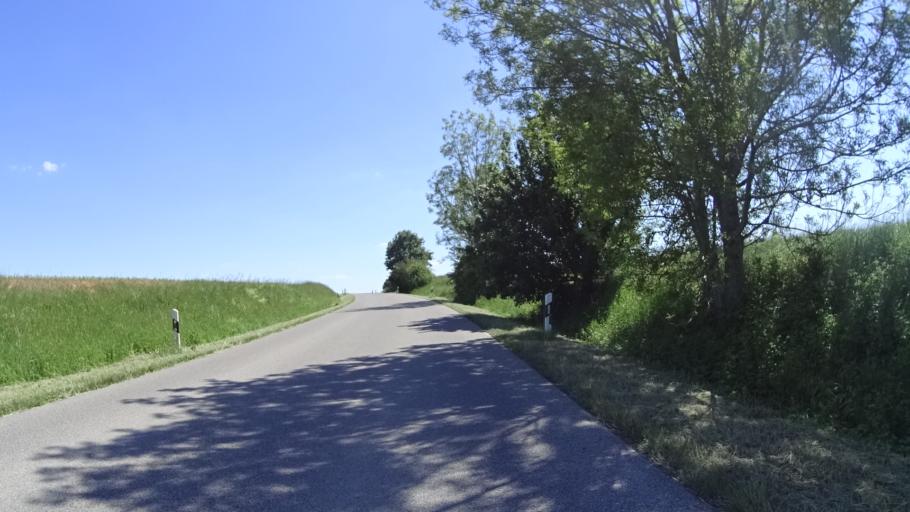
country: DE
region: Bavaria
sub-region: Regierungsbezirk Mittelfranken
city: Gebsattel
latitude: 49.3599
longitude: 10.1923
